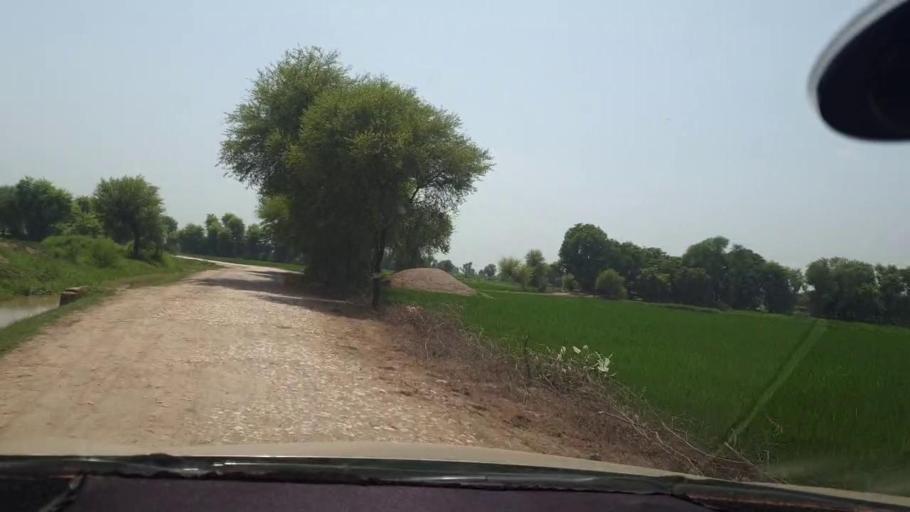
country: PK
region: Sindh
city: Kambar
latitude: 27.6682
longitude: 67.9432
